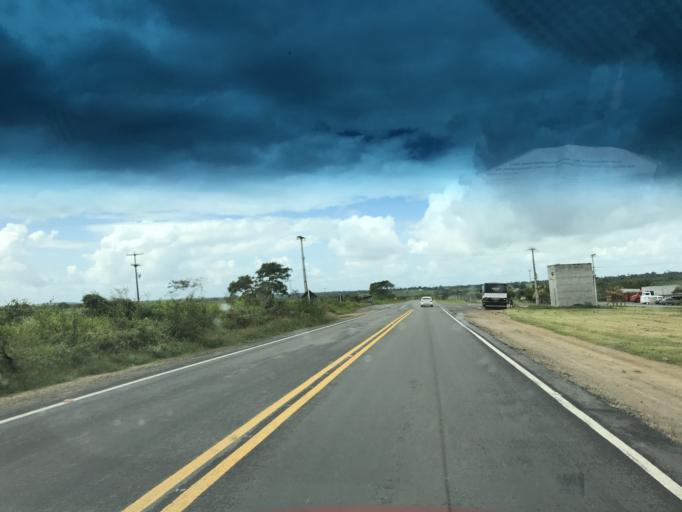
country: BR
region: Bahia
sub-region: Conceicao Do Almeida
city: Conceicao do Almeida
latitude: -12.6776
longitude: -39.2607
